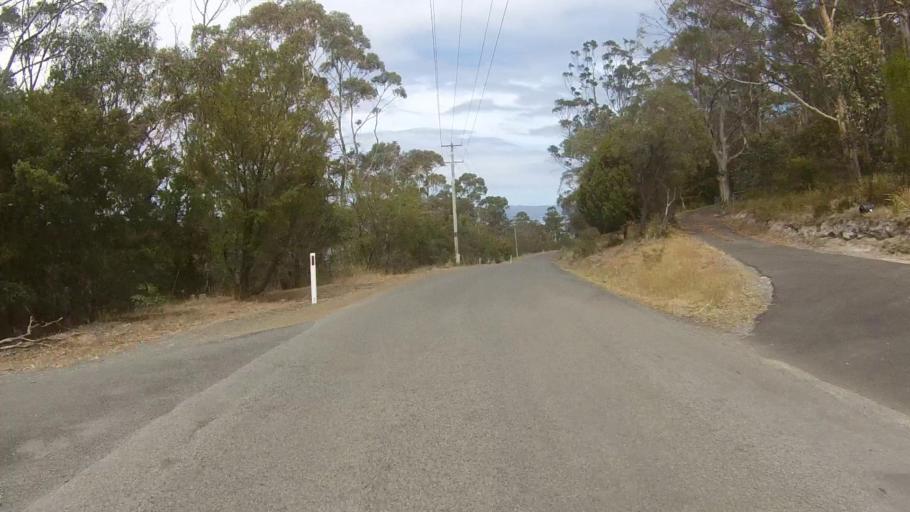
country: AU
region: Tasmania
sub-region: Kingborough
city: Blackmans Bay
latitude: -43.0509
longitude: 147.3405
